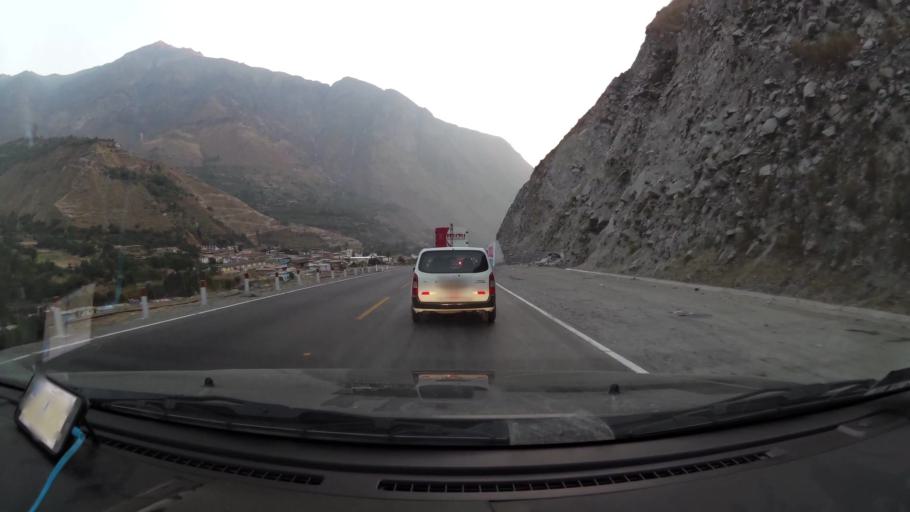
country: PE
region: Lima
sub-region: Provincia de Huarochiri
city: Surco
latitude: -11.8810
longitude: -76.4369
